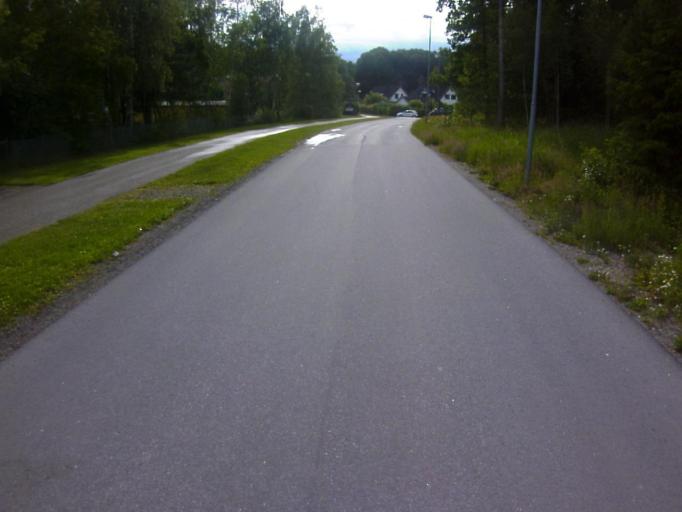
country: SE
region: Soedermanland
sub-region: Eskilstuna Kommun
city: Skogstorp
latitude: 59.3606
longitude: 16.4694
